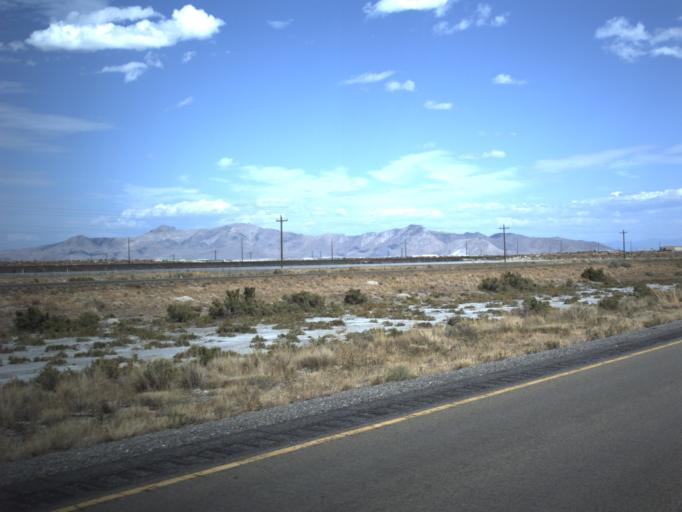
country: US
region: Utah
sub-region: Tooele County
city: Grantsville
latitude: 40.7482
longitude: -112.6784
